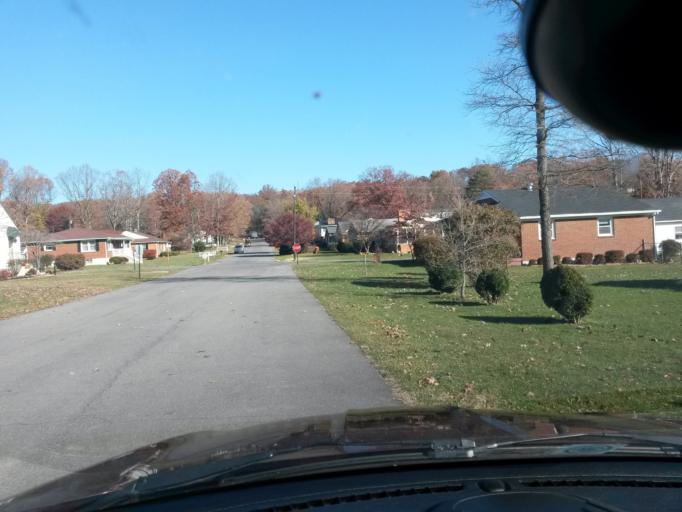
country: US
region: Virginia
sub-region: Alleghany County
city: Clifton Forge
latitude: 37.8273
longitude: -79.8219
